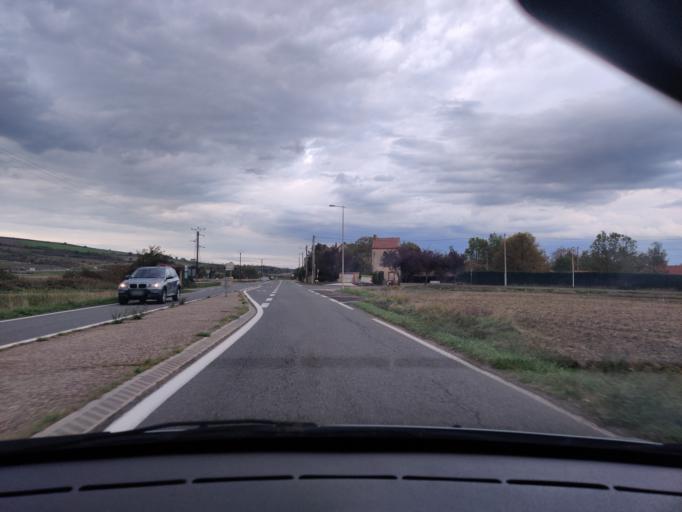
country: FR
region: Auvergne
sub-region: Departement du Puy-de-Dome
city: Saint-Bonnet-pres-Riom
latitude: 45.9561
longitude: 3.1071
